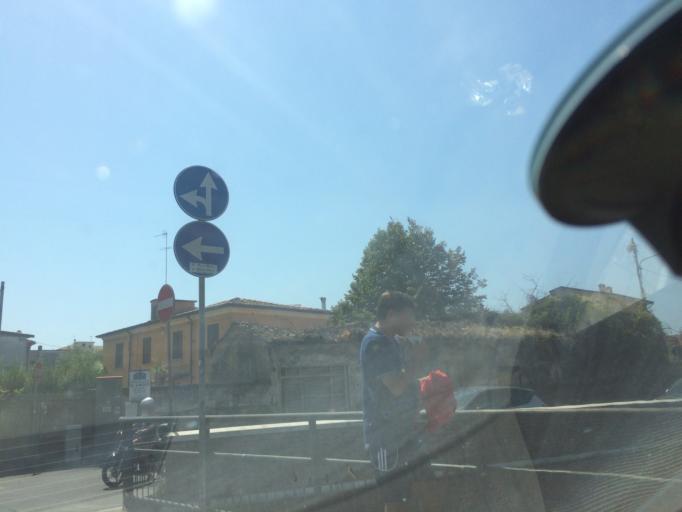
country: IT
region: Tuscany
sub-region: Provincia di Massa-Carrara
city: Massa
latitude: 44.0106
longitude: 10.0988
